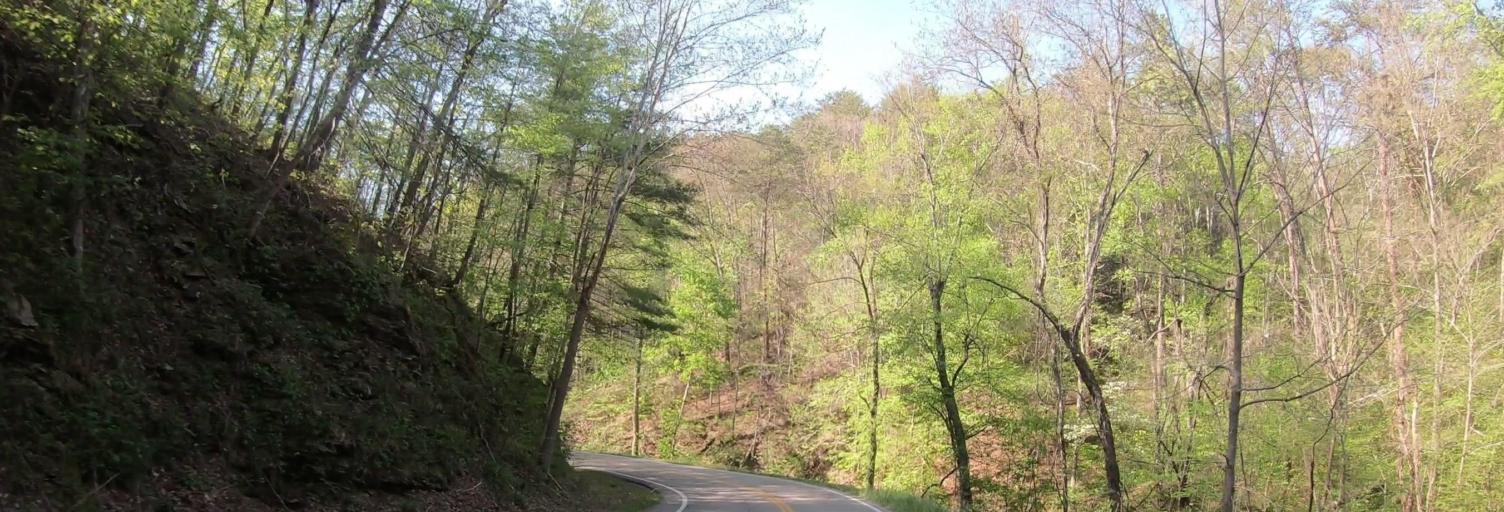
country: US
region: Tennessee
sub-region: Loudon County
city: Greenback
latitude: 35.5193
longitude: -83.9893
